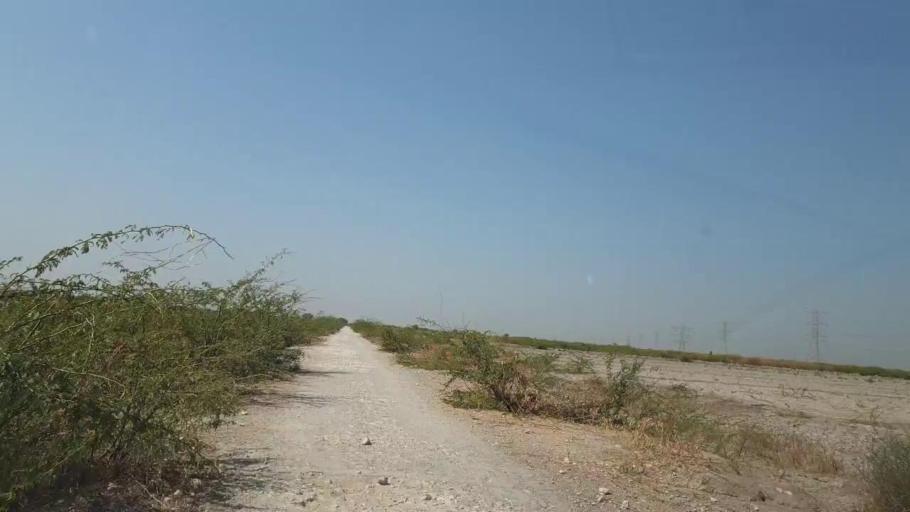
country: PK
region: Sindh
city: Kunri
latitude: 25.0965
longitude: 69.4770
